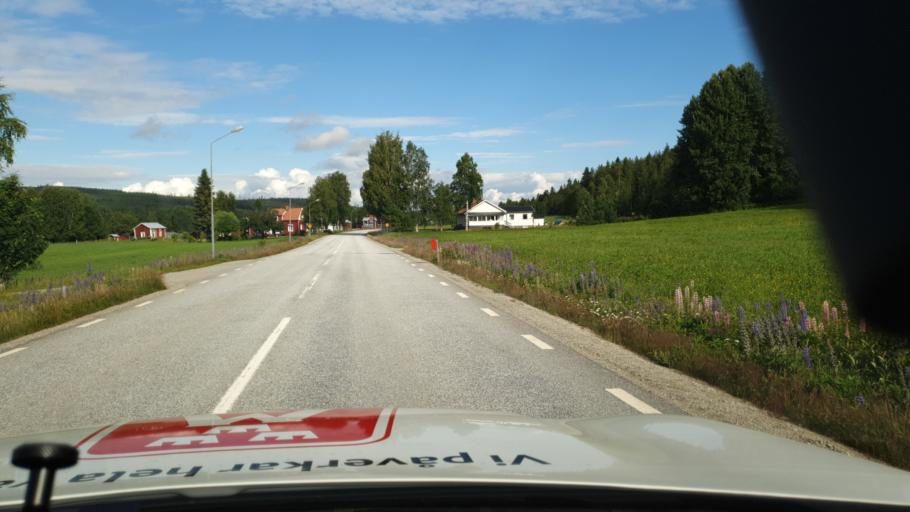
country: SE
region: Vaesterbotten
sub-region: Vindelns Kommun
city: Vindeln
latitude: 64.1361
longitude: 19.5268
